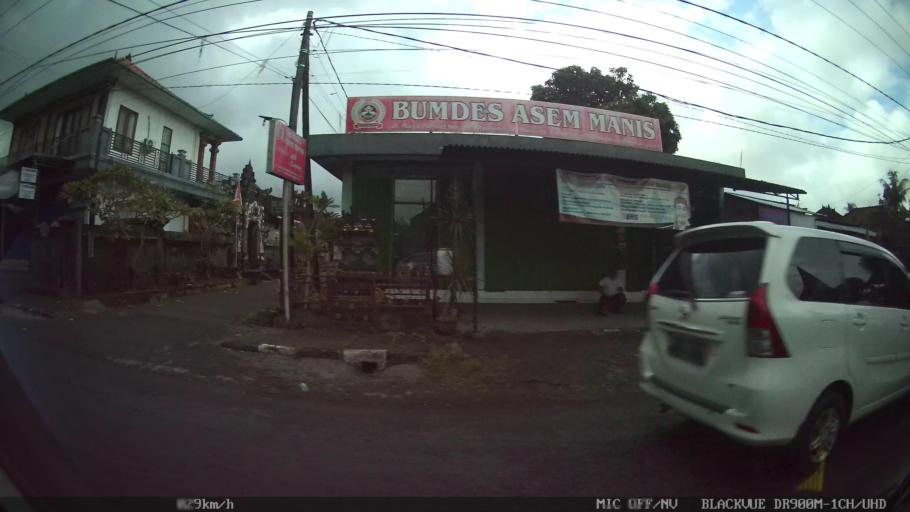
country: ID
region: Bali
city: Banjar Keraman
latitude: -8.5285
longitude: 115.2122
